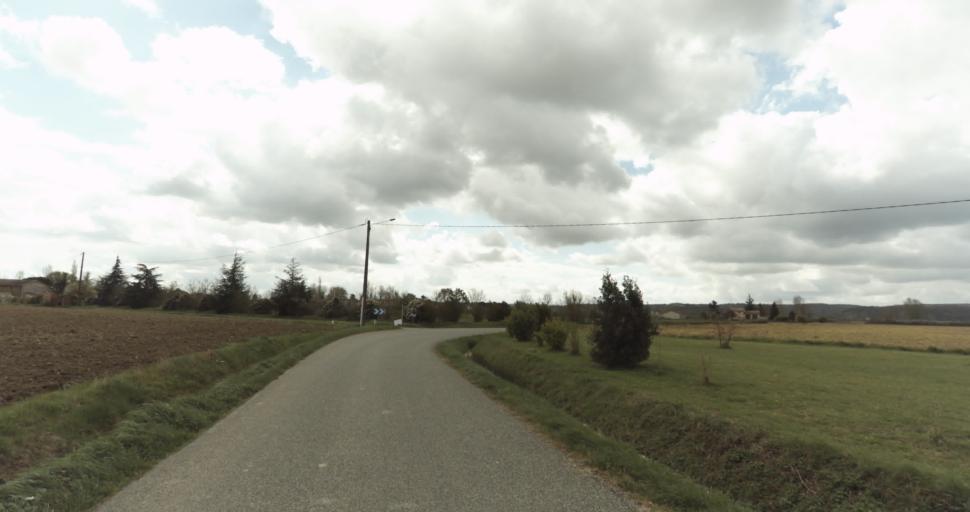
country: FR
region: Midi-Pyrenees
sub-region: Departement de la Haute-Garonne
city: Auterive
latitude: 43.3296
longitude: 1.4701
